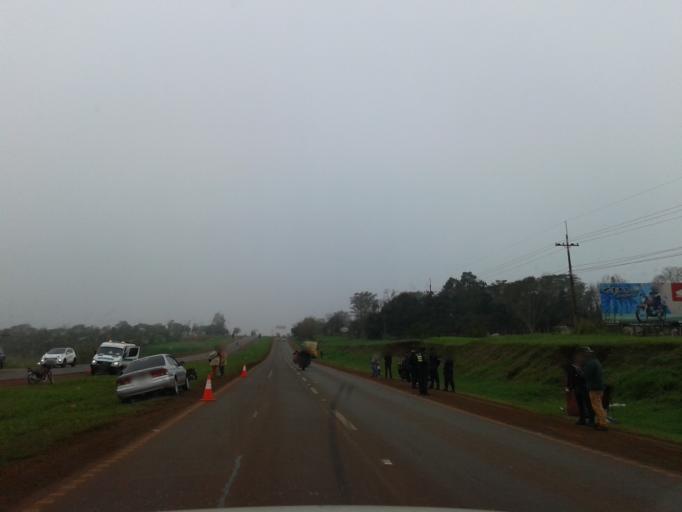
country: PY
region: Alto Parana
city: Colonia Yguazu
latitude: -25.4863
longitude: -54.8694
